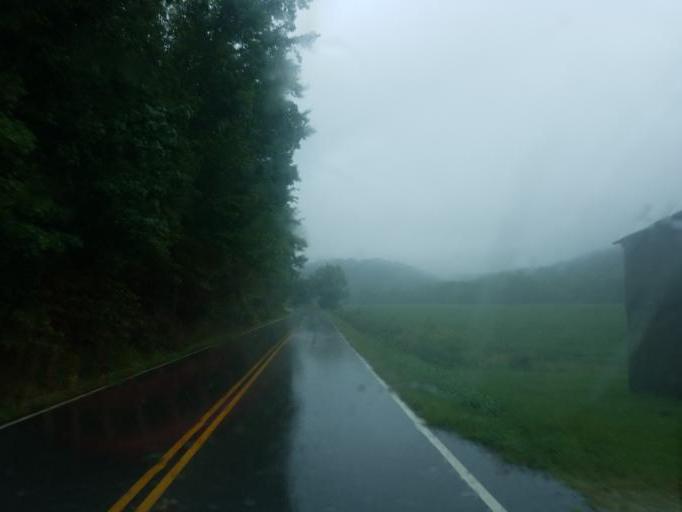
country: US
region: Kentucky
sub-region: Carter County
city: Grayson
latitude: 38.4706
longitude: -83.0419
